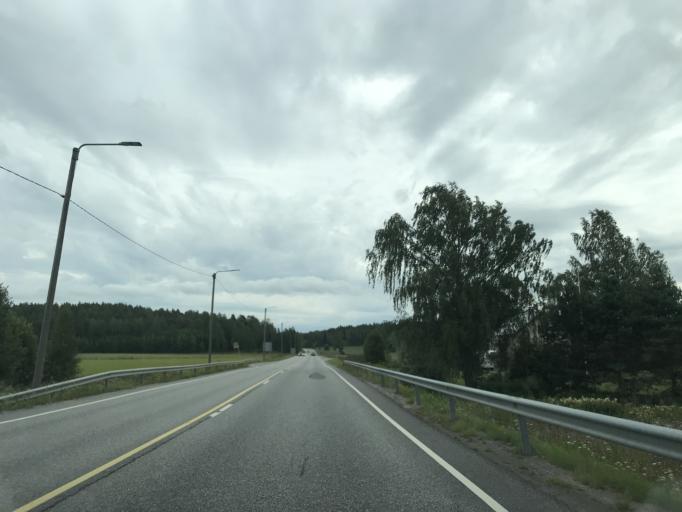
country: FI
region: Varsinais-Suomi
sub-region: Turku
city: Piikkioe
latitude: 60.4342
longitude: 22.5909
